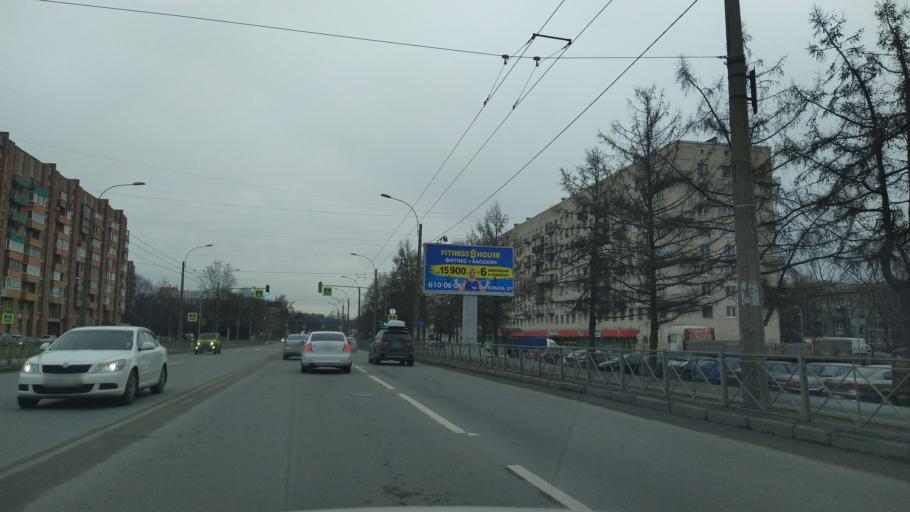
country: RU
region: St.-Petersburg
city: Sosnovka
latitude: 60.0084
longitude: 30.3511
